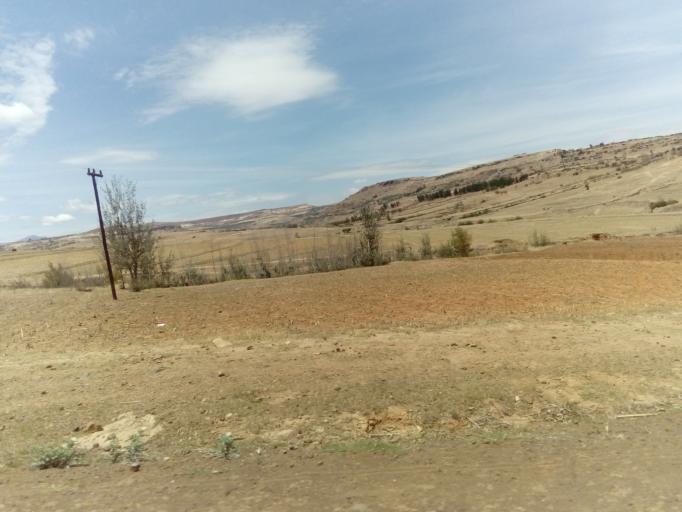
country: LS
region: Berea
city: Teyateyaneng
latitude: -29.0908
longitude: 27.9312
